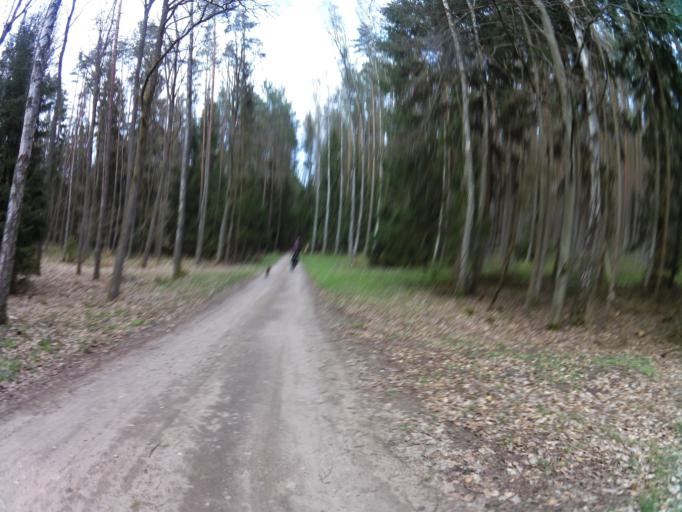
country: PL
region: West Pomeranian Voivodeship
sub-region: Powiat szczecinecki
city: Szczecinek
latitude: 53.8306
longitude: 16.6571
